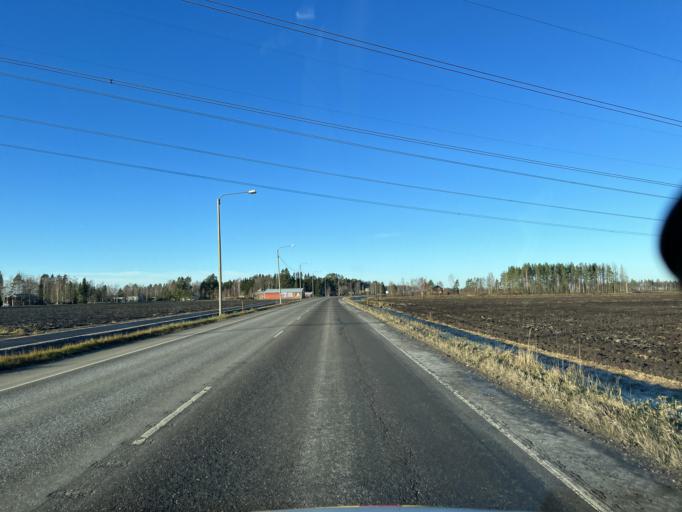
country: FI
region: Northern Ostrobothnia
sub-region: Nivala-Haapajaervi
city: Nivala
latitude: 63.9537
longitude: 24.8697
